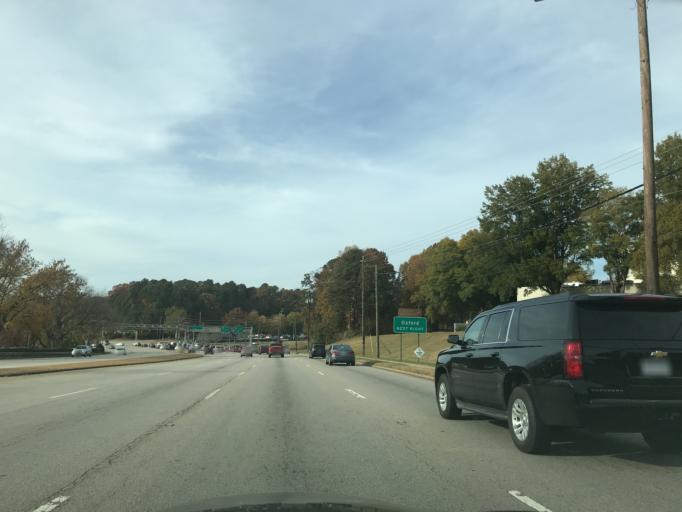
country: US
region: North Carolina
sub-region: Wake County
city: West Raleigh
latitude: 35.8416
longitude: -78.6785
